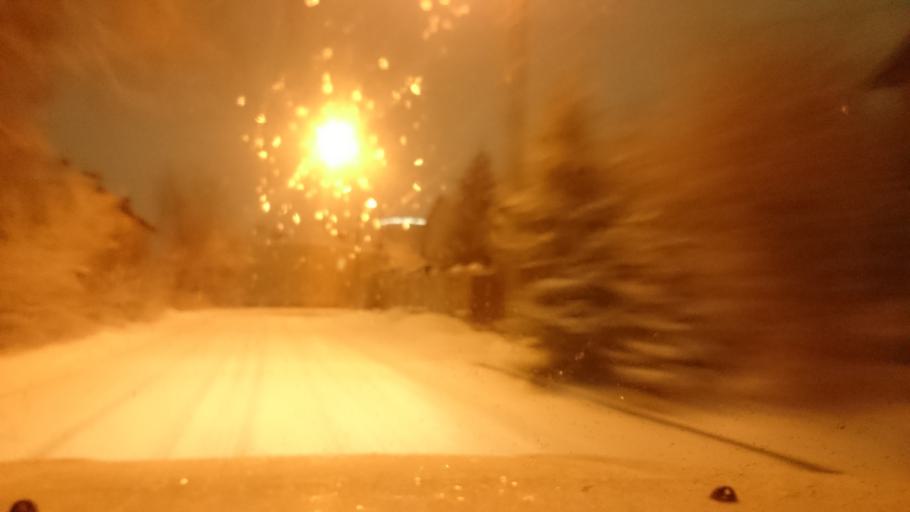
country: RU
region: Tula
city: Tula
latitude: 54.1870
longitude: 37.5696
